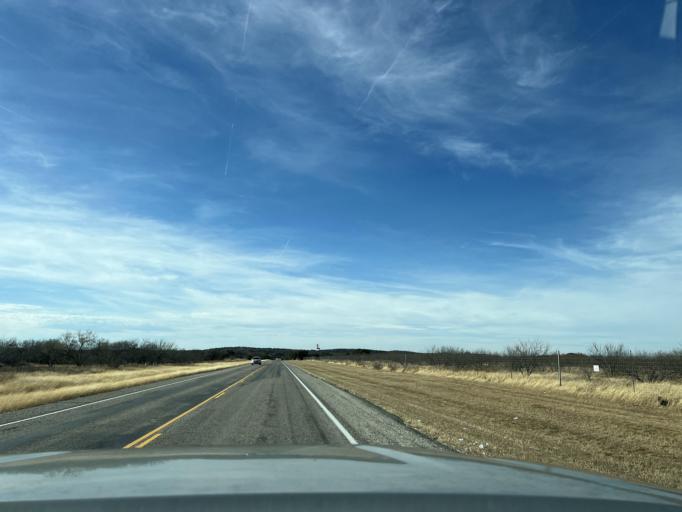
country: US
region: Texas
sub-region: Eastland County
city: Cisco
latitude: 32.4597
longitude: -98.9973
